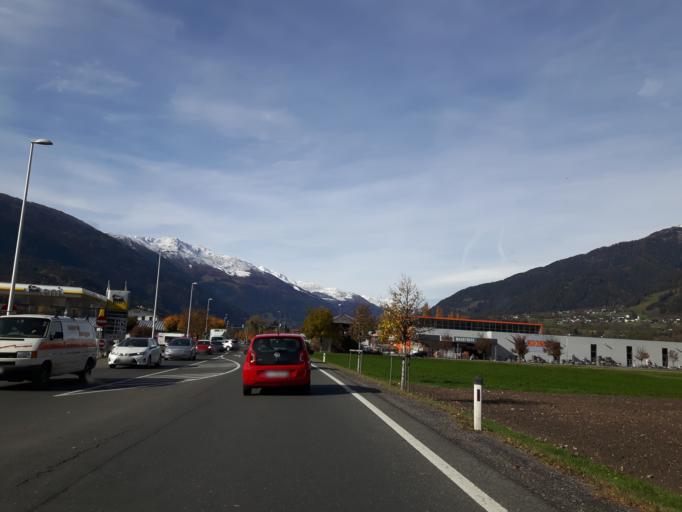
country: AT
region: Tyrol
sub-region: Politischer Bezirk Lienz
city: Lienz
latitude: 46.8312
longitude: 12.7840
